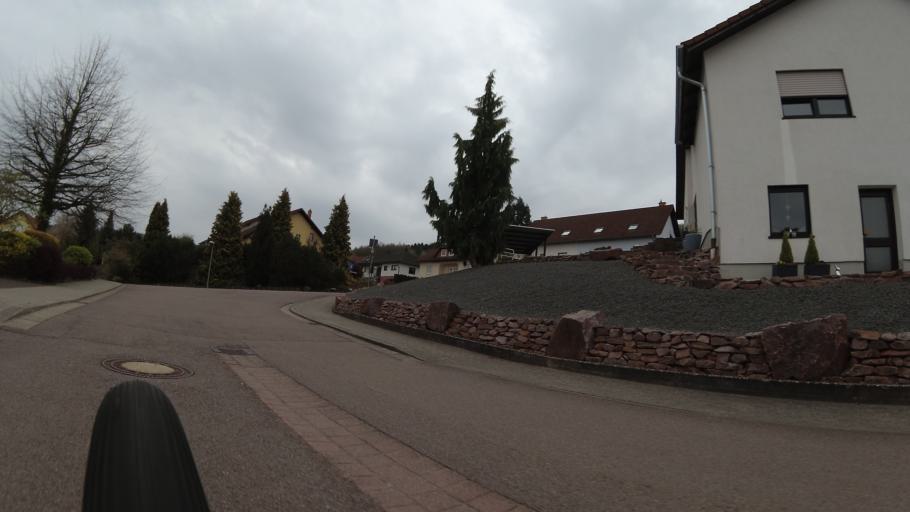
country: DE
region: Saarland
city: Merzig
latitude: 49.4489
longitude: 6.6676
